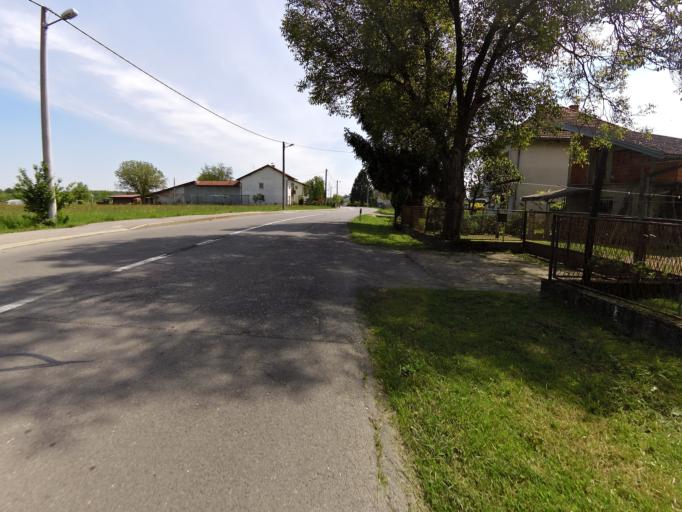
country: HR
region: Karlovacka
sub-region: Grad Karlovac
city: Karlovac
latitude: 45.5405
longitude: 15.5379
